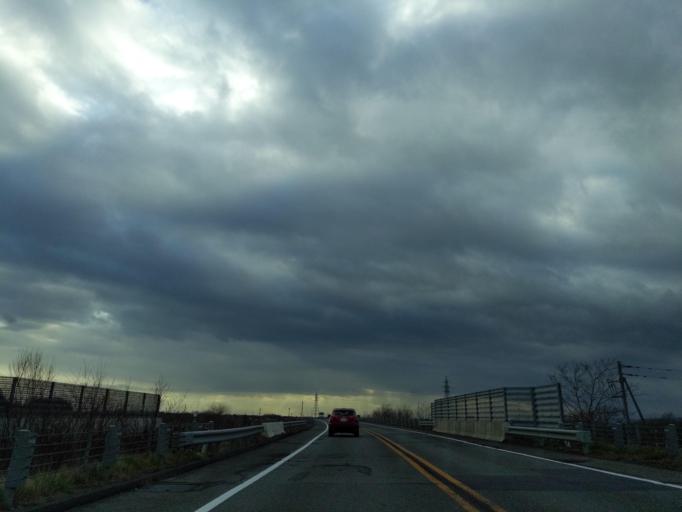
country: JP
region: Hokkaido
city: Chitose
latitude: 42.8431
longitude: 141.6952
